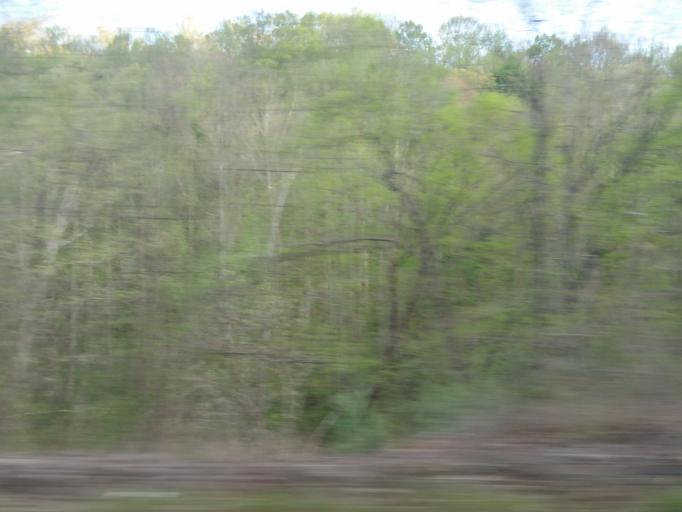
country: US
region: Kentucky
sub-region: Bell County
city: Middlesboro
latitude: 36.5793
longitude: -83.9115
